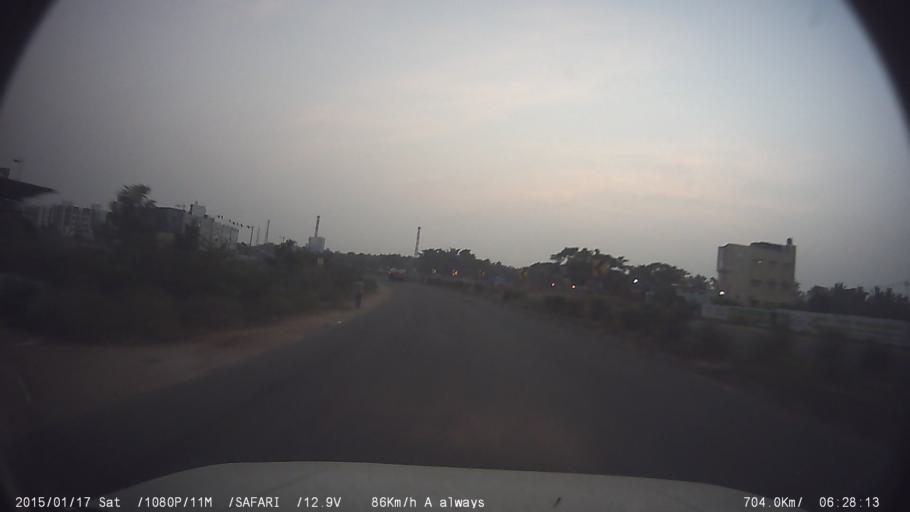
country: IN
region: Tamil Nadu
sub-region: Kancheepuram
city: Sriperumbudur
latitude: 12.9336
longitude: 79.9067
